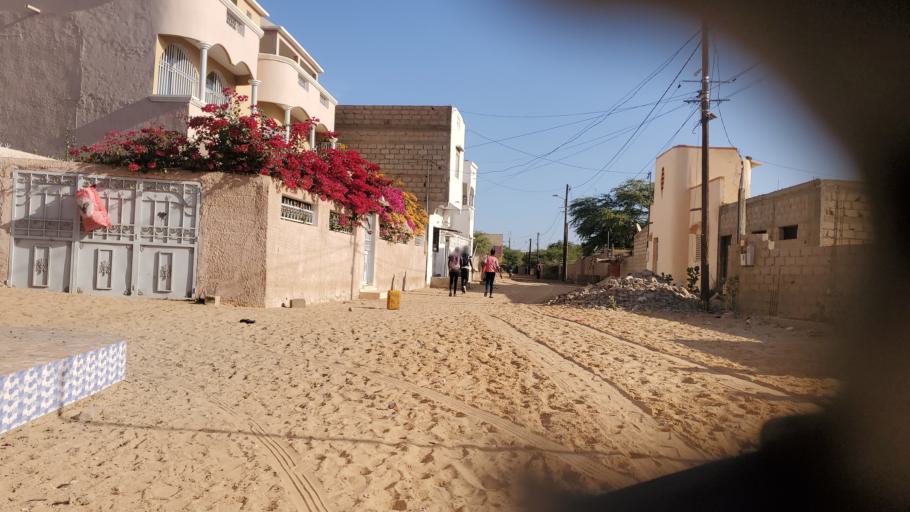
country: SN
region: Saint-Louis
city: Saint-Louis
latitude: 16.0580
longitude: -16.4216
